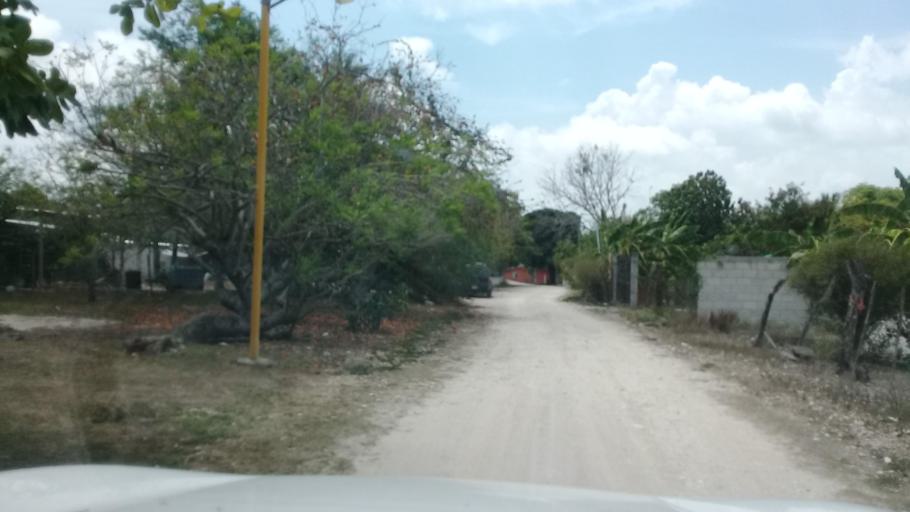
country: MX
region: Veracruz
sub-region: Emiliano Zapata
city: Plan del Rio
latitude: 19.3545
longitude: -96.6464
